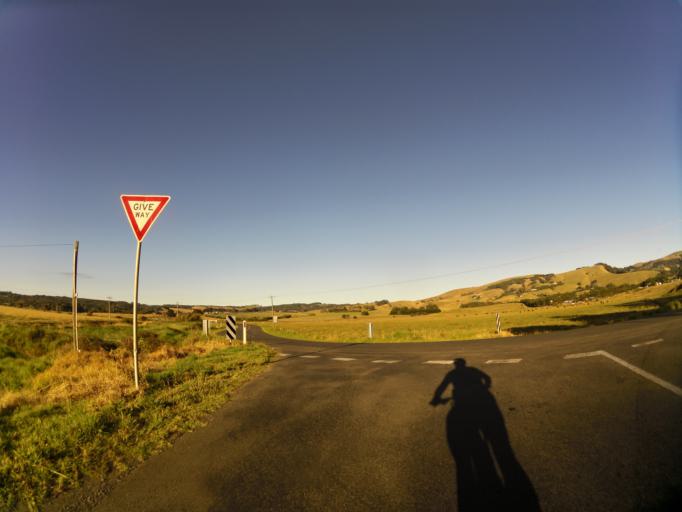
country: AU
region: Victoria
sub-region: Colac-Otway
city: Apollo Bay
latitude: -38.7606
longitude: 143.6632
